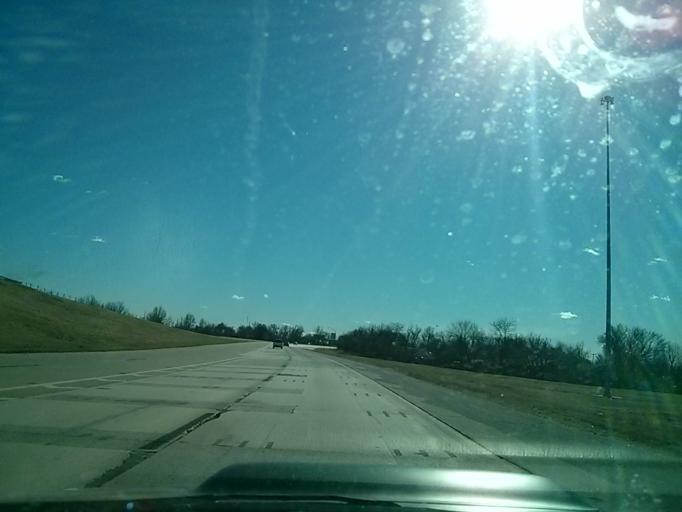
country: US
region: Oklahoma
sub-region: Tulsa County
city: Turley
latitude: 36.1981
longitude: -95.9513
